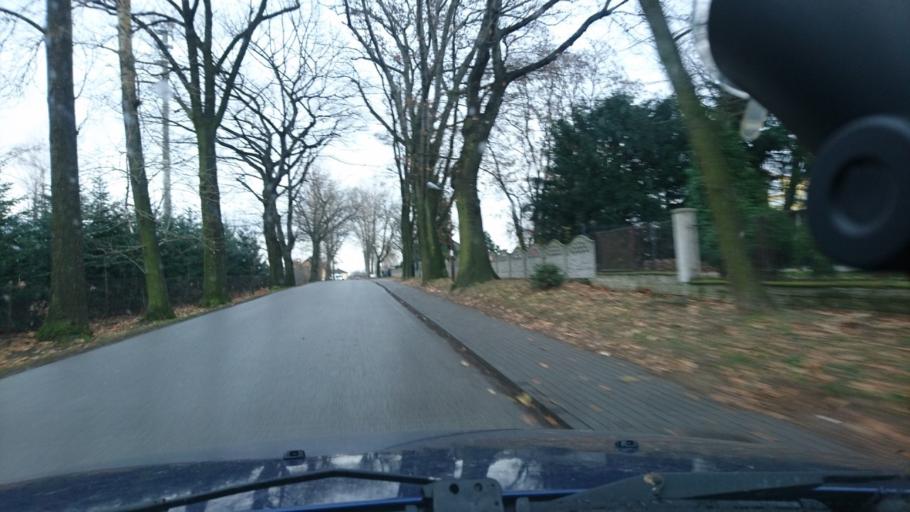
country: PL
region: Silesian Voivodeship
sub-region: Powiat bielski
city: Bestwinka
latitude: 49.9199
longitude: 19.0536
